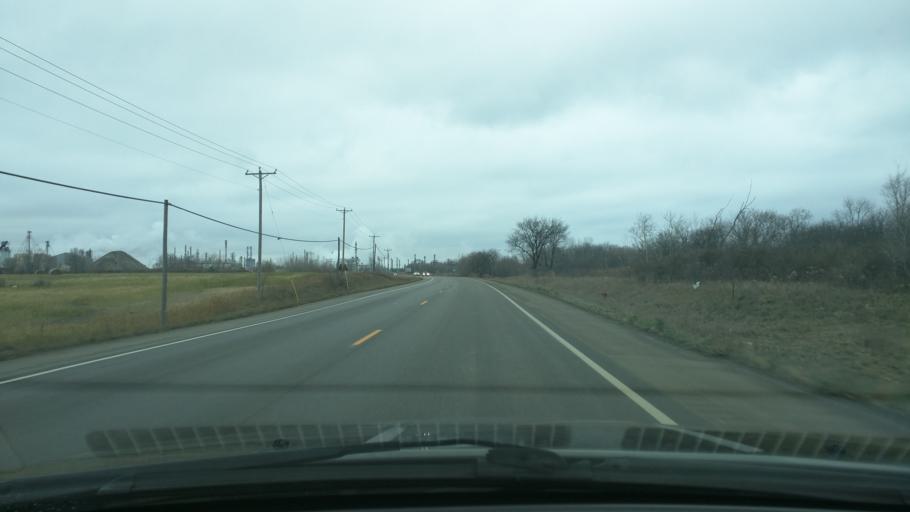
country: US
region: Minnesota
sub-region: Washington County
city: Saint Paul Park
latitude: 44.7587
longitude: -93.0170
